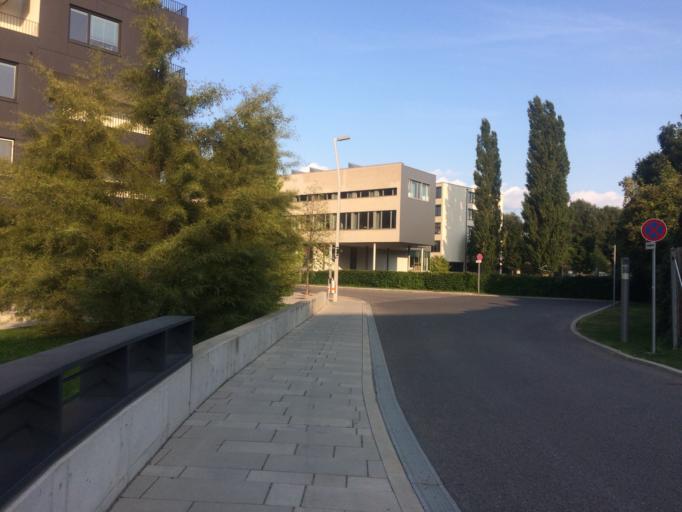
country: AT
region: Vienna
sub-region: Wien Stadt
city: Vienna
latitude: 48.2121
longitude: 16.4160
